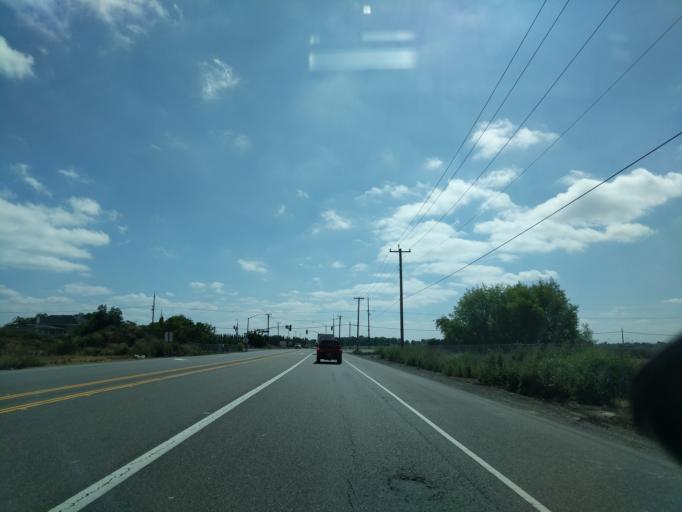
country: US
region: California
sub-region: Contra Costa County
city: Byron
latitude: 37.8964
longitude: -121.6434
